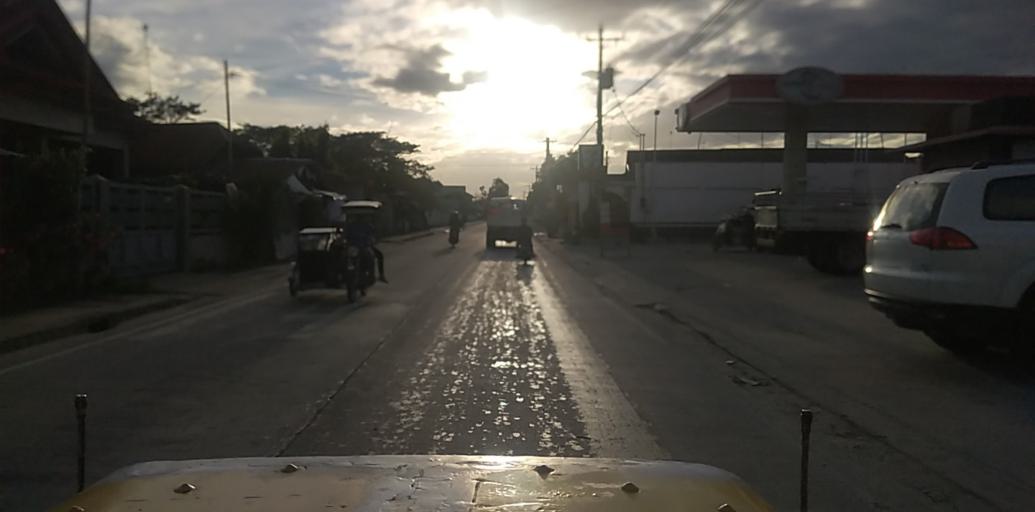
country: PH
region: Central Luzon
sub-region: Province of Pampanga
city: Malino
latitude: 15.1264
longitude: 120.6722
